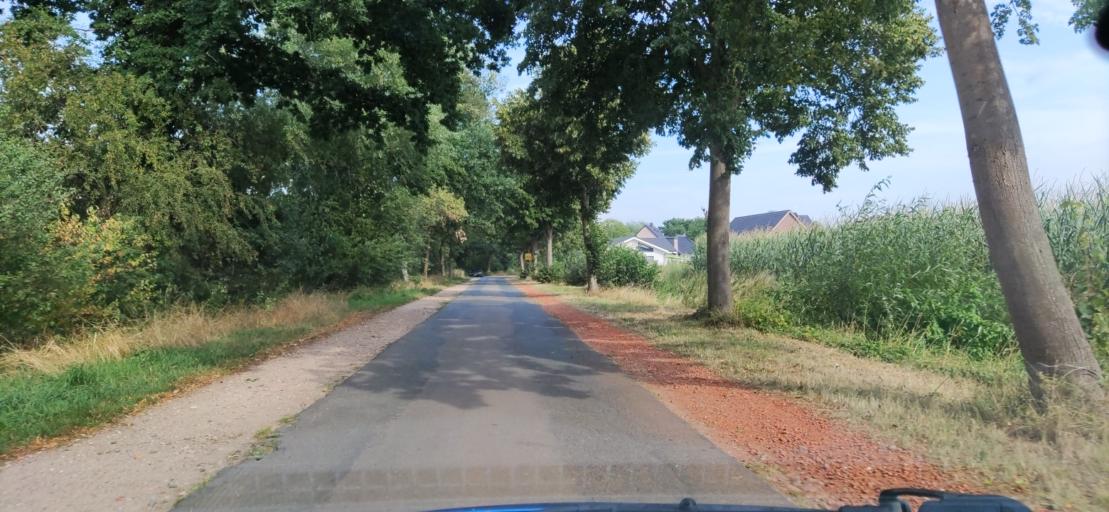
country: DE
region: Lower Saxony
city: Bleckede
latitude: 53.2889
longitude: 10.7196
